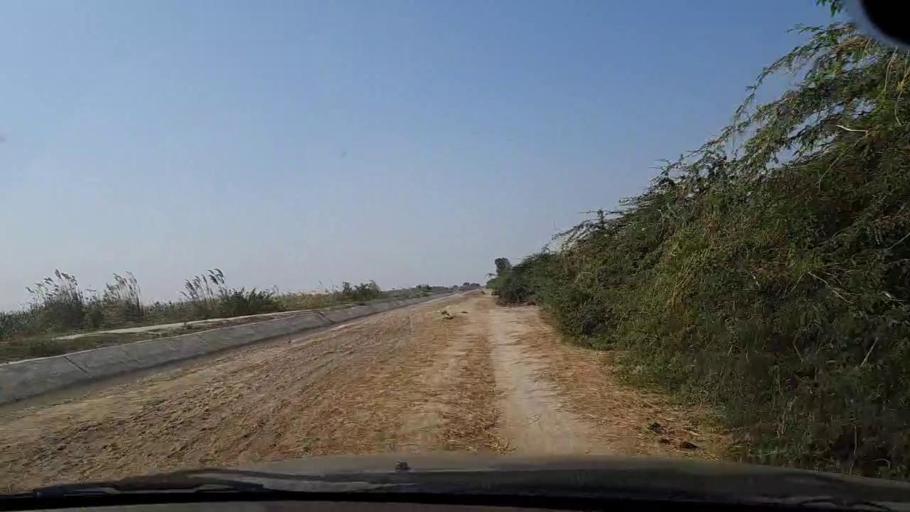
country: PK
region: Sindh
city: Chuhar Jamali
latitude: 24.4274
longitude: 67.8107
